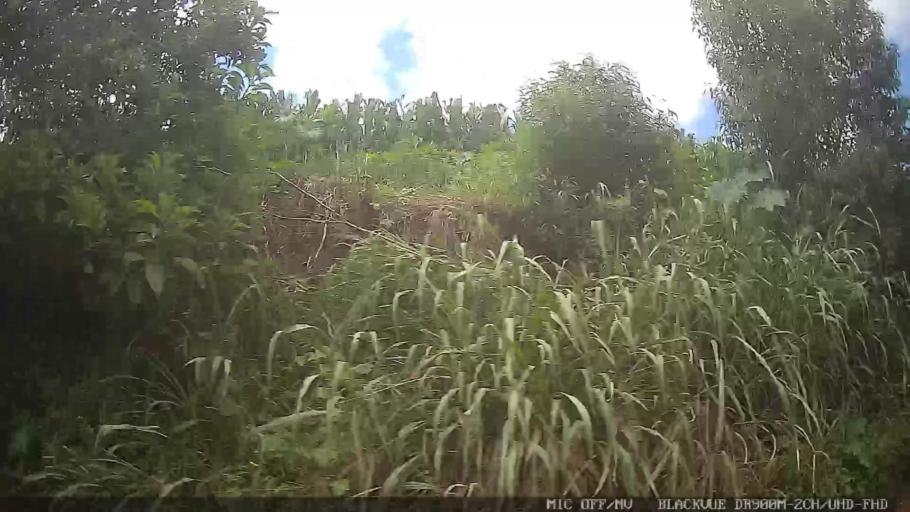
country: BR
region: Sao Paulo
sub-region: Braganca Paulista
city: Braganca Paulista
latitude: -22.8638
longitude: -46.6944
